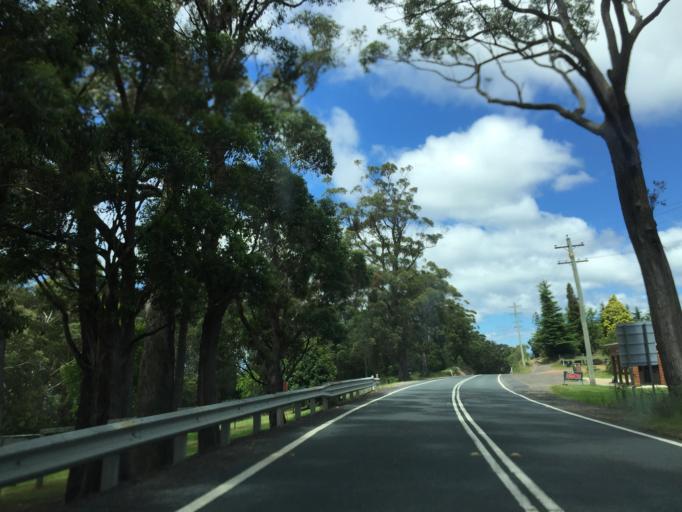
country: AU
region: New South Wales
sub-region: Blue Mountains Municipality
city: Hazelbrook
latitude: -33.5118
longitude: 150.4930
